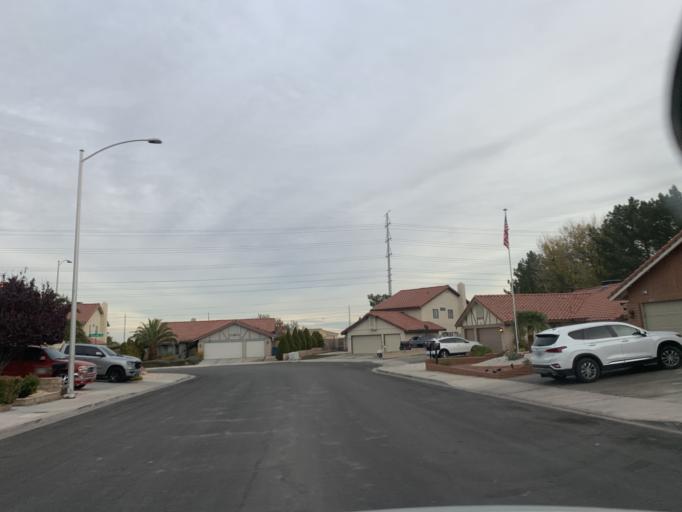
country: US
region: Nevada
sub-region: Clark County
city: Spring Valley
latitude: 36.1532
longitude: -115.2810
